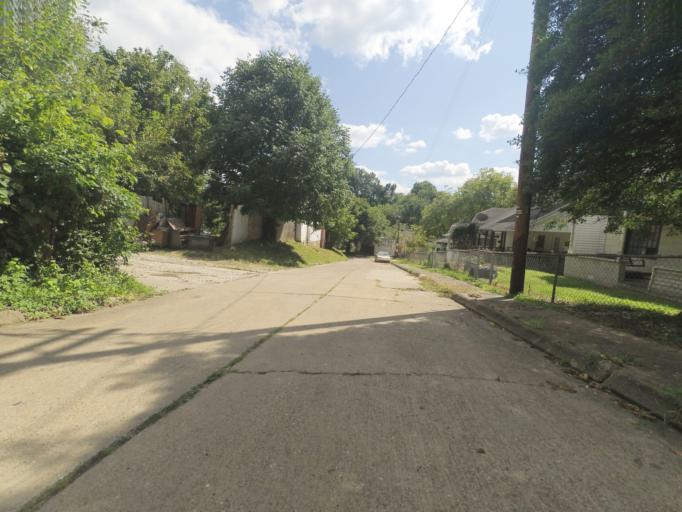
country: US
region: West Virginia
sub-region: Cabell County
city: Huntington
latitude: 38.4094
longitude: -82.4219
